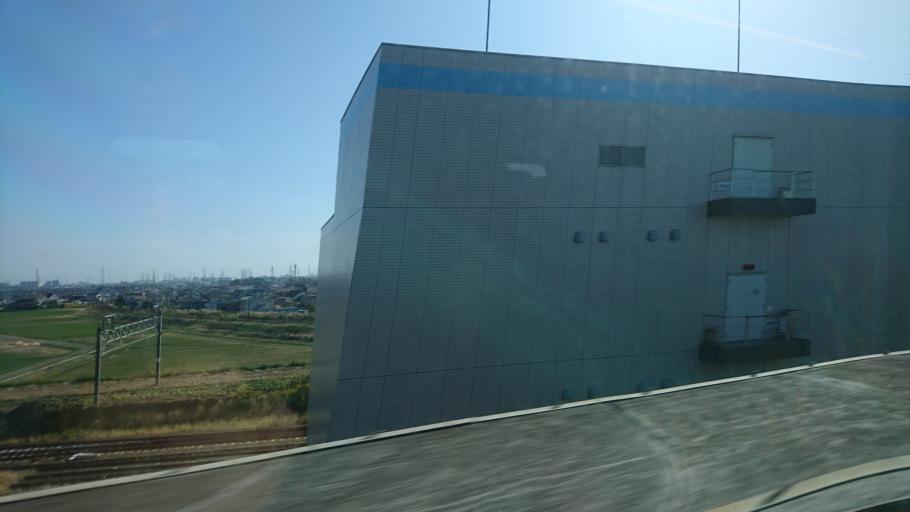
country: JP
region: Miyagi
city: Rifu
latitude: 38.3025
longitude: 140.9579
